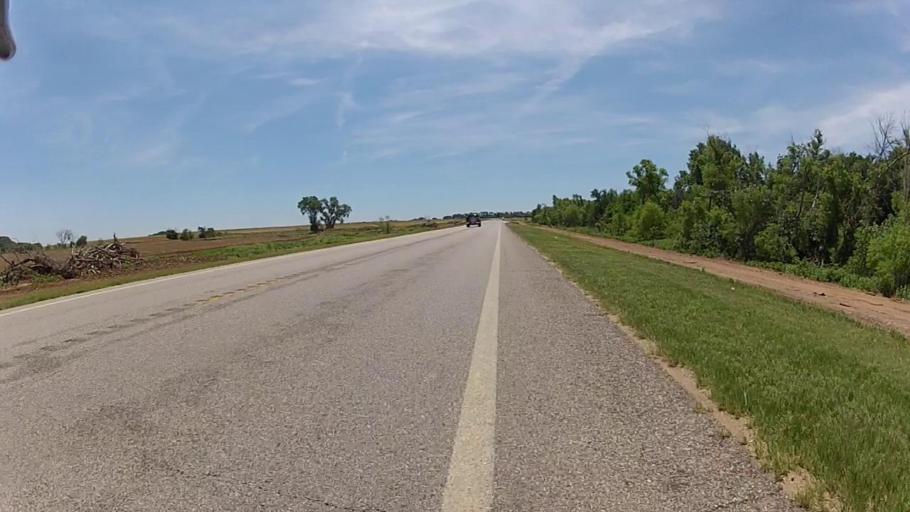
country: US
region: Kansas
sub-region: Barber County
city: Medicine Lodge
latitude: 37.2620
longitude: -98.5299
